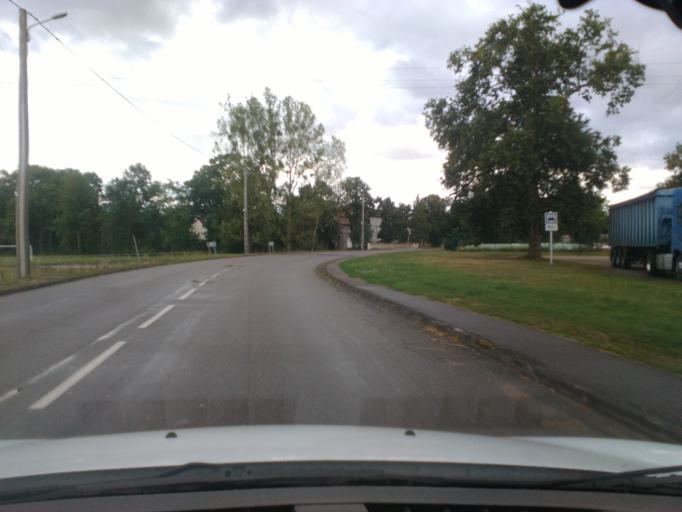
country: FR
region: Lorraine
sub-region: Departement des Vosges
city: Mirecourt
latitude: 48.3935
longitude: 6.1329
